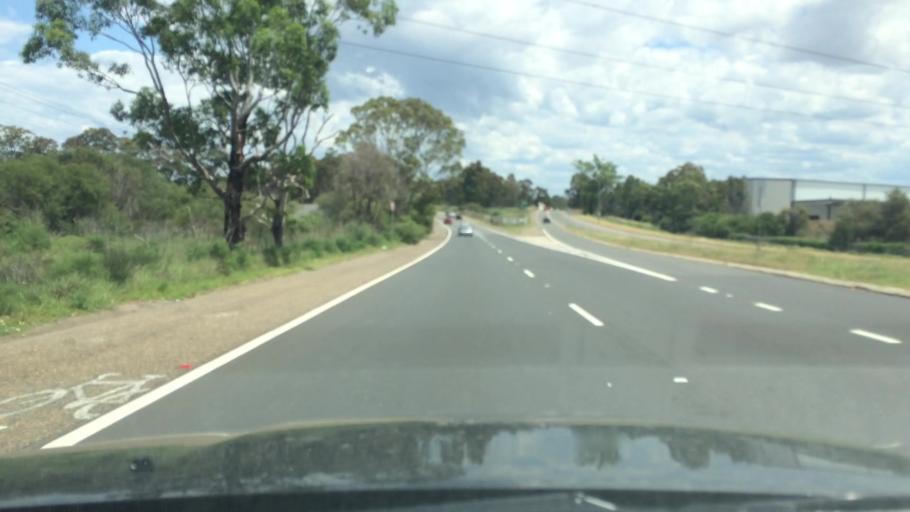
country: AU
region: New South Wales
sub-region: Campbelltown Municipality
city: Glenfield
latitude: -33.9644
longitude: 150.8788
